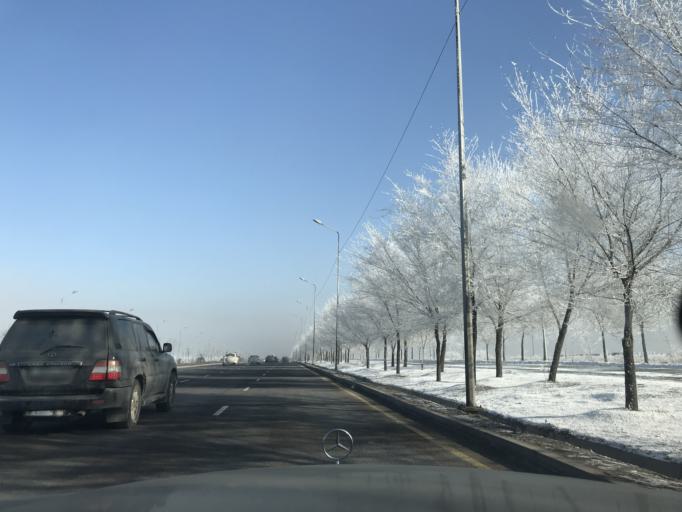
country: KZ
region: Almaty Oblysy
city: Burunday
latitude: 43.2911
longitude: 76.8291
